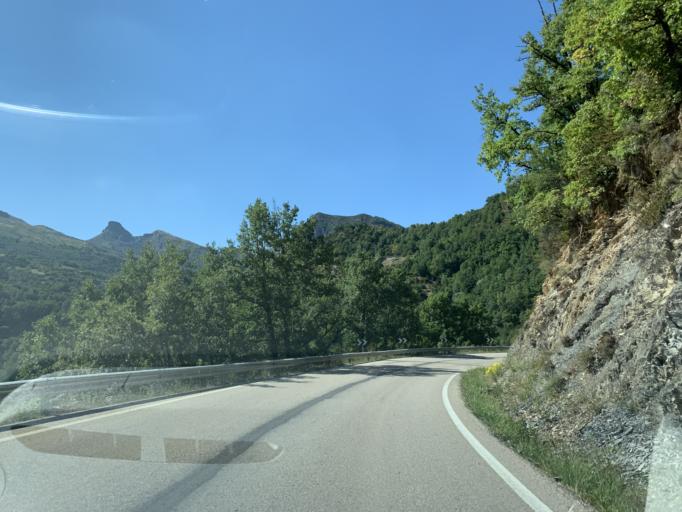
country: ES
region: Aragon
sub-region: Provincia de Huesca
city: Hoz de Jaca
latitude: 42.7282
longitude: -0.3018
